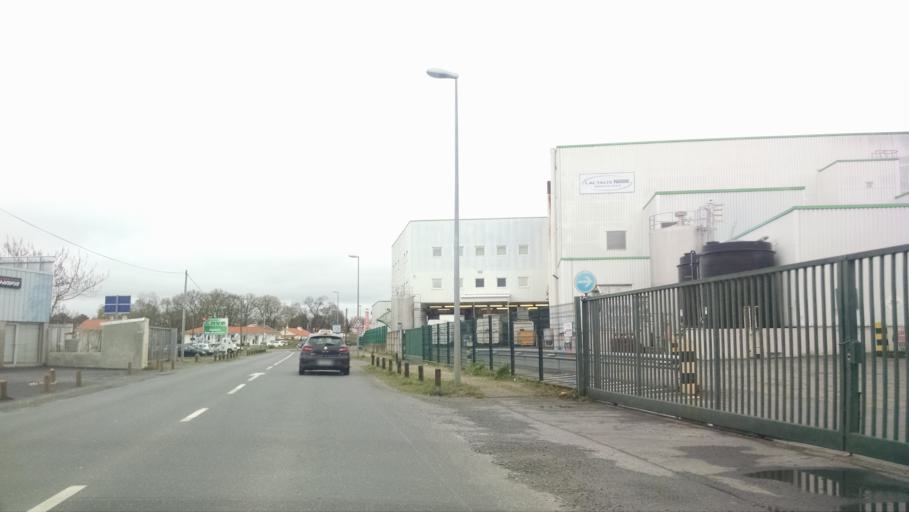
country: FR
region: Pays de la Loire
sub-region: Departement de la Loire-Atlantique
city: Vallet
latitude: 47.1628
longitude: -1.2752
